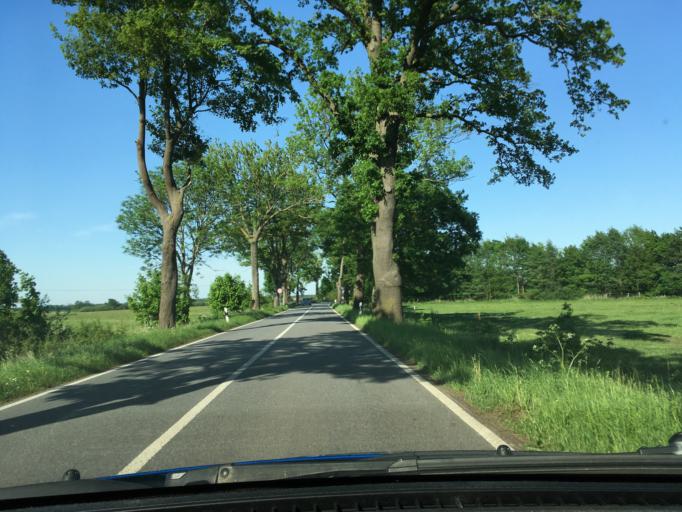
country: DE
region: Brandenburg
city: Lenzen
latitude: 53.0825
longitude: 11.4177
